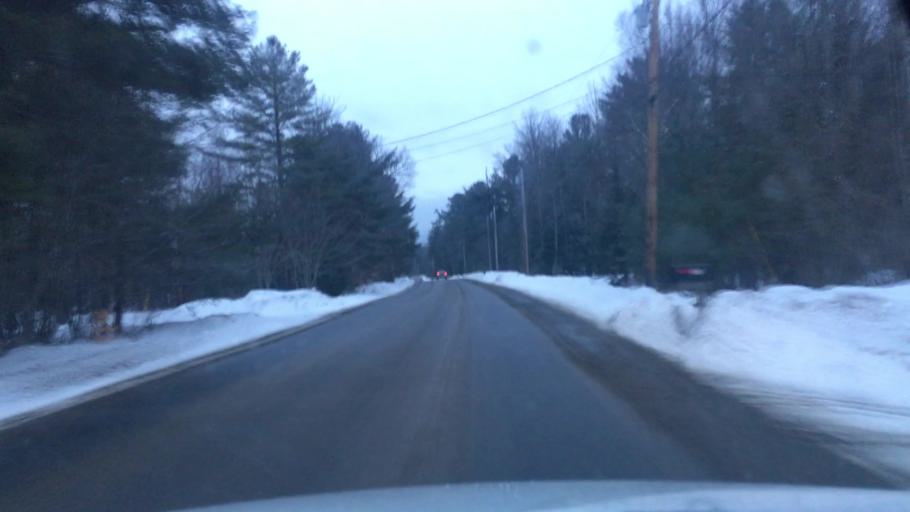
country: US
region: Maine
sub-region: Kennebec County
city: Oakland
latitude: 44.6245
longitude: -69.7279
